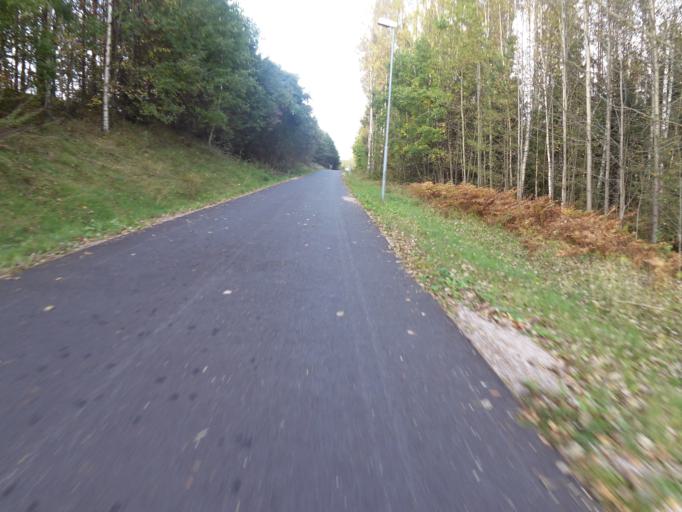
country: FI
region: Uusimaa
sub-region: Helsinki
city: Kauniainen
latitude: 60.2556
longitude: 24.7188
